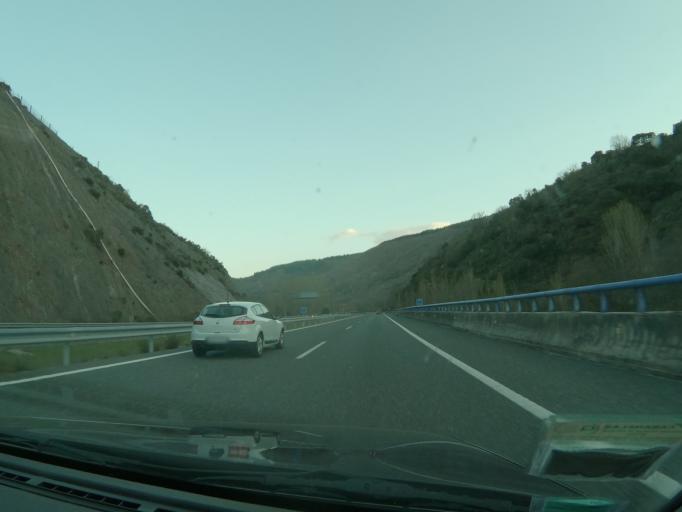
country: ES
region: Castille and Leon
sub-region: Provincia de Leon
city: Trabadelo
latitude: 42.6344
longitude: -6.8525
